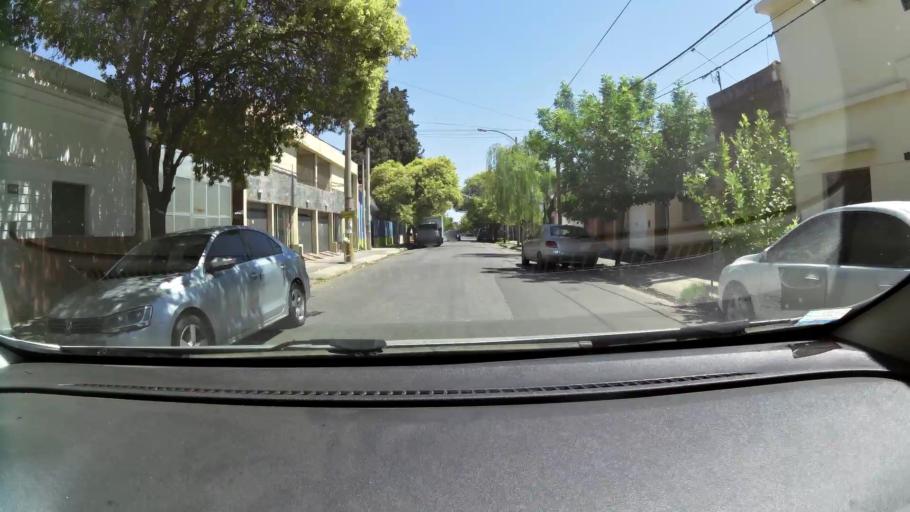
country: AR
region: Cordoba
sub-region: Departamento de Capital
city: Cordoba
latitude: -31.3880
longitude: -64.1599
